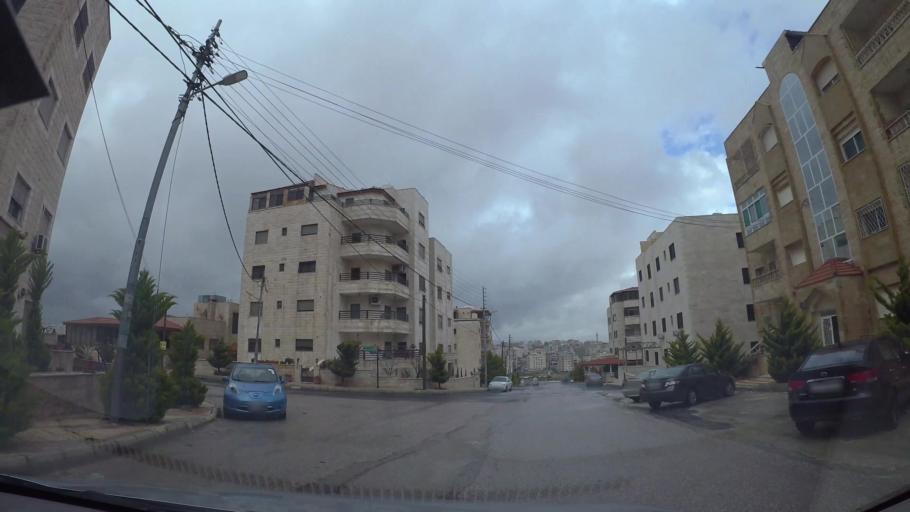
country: JO
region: Amman
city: Al Jubayhah
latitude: 32.0364
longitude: 35.8861
